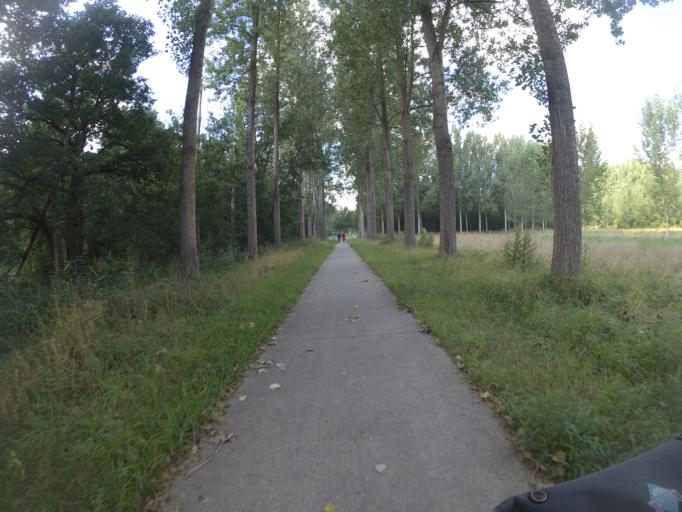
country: NL
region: North Brabant
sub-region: Gemeente Veghel
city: Eerde
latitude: 51.6301
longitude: 5.4738
